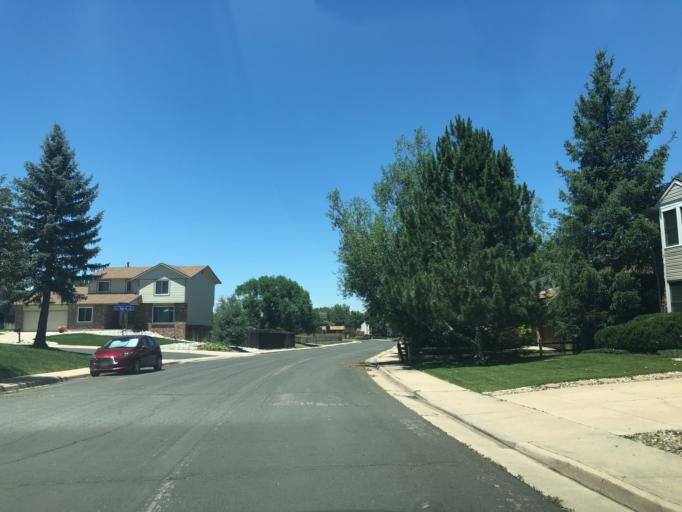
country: US
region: Colorado
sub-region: Arapahoe County
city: Dove Valley
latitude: 39.6178
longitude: -104.7770
